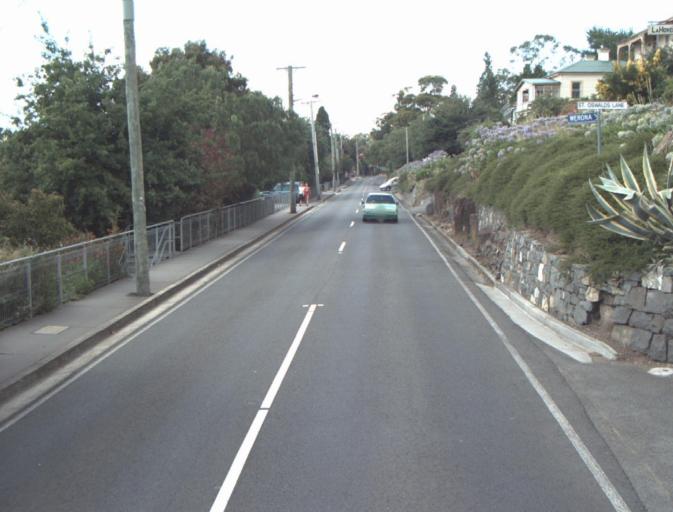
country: AU
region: Tasmania
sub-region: Launceston
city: Launceston
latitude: -41.4356
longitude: 147.1228
